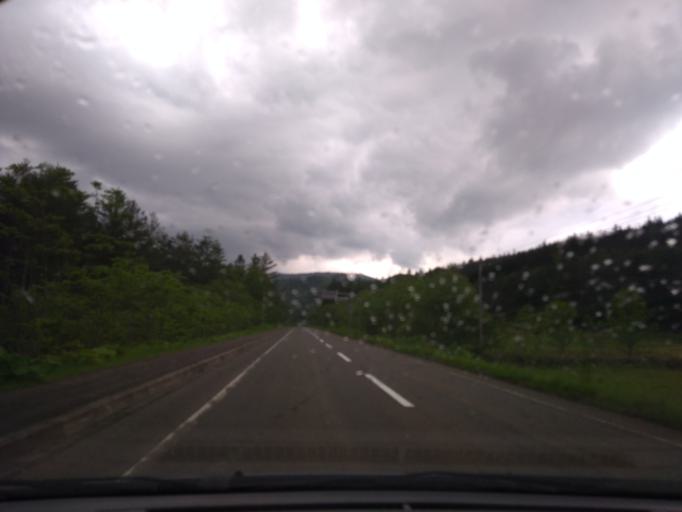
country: JP
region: Hokkaido
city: Shimo-furano
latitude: 43.1269
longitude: 142.4103
